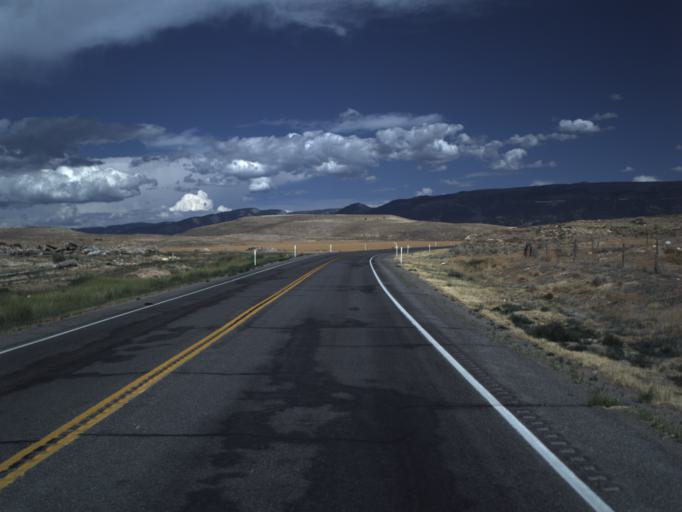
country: US
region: Utah
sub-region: Sanpete County
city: Gunnison
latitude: 39.1610
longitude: -111.7941
